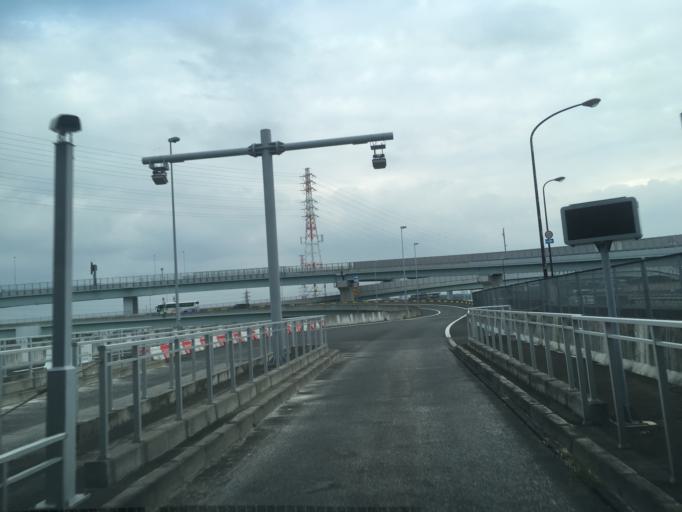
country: JP
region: Kanagawa
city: Chigasaki
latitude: 35.3491
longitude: 139.3911
